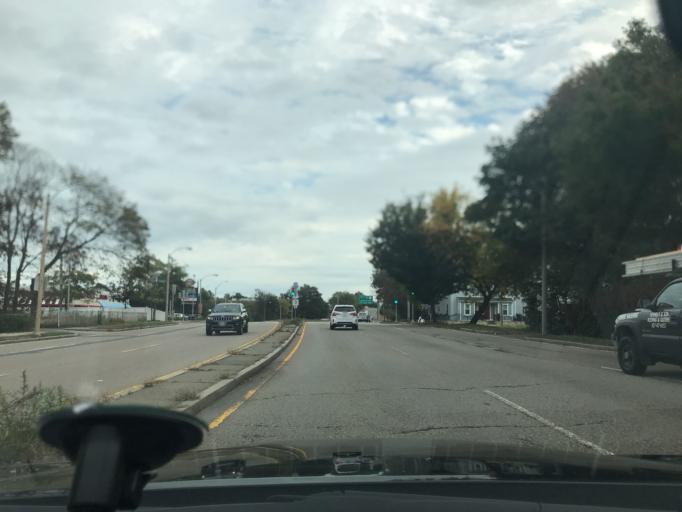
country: US
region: Massachusetts
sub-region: Suffolk County
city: South Boston
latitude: 42.2906
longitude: -71.0464
